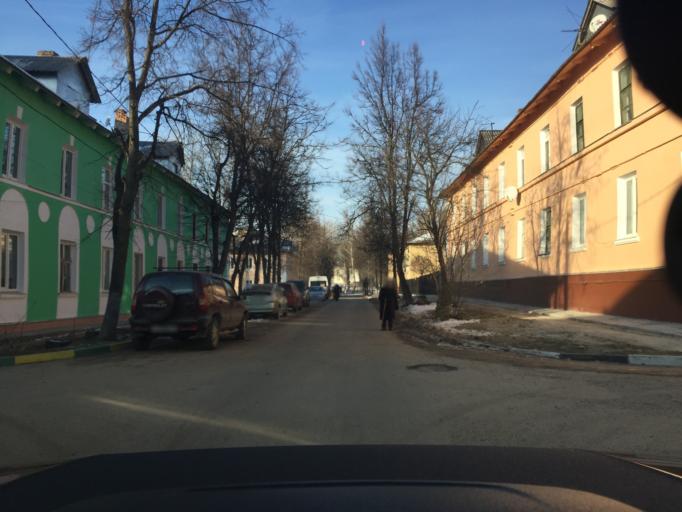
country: RU
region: Tula
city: Tula
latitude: 54.1828
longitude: 37.7043
